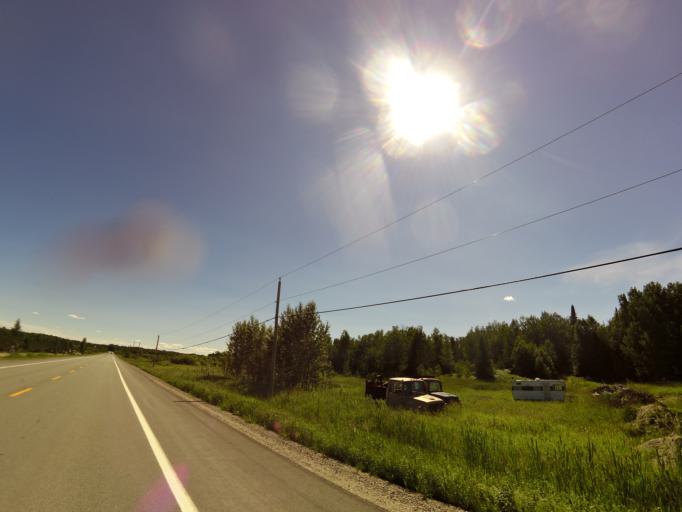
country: CA
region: Quebec
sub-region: Abitibi-Temiscamingue
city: Senneterre
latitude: 48.2089
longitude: -77.3563
